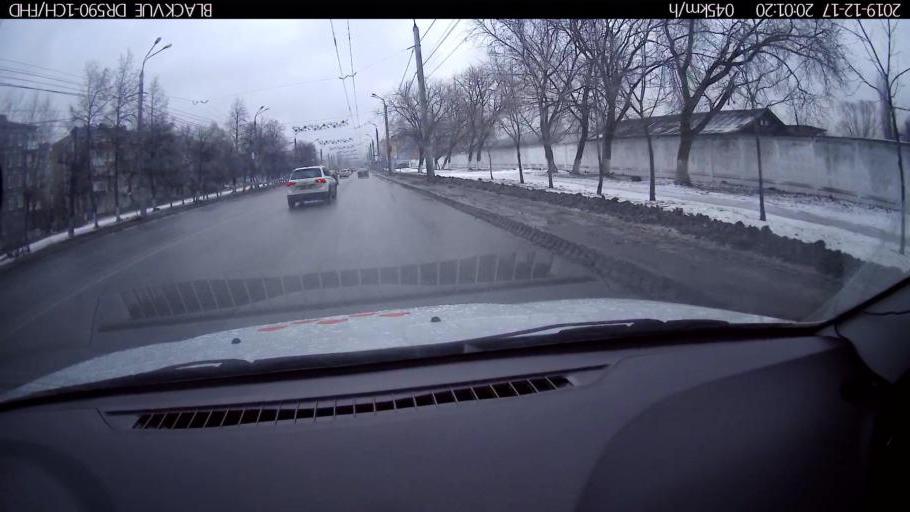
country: RU
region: Nizjnij Novgorod
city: Nizhniy Novgorod
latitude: 56.3228
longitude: 43.9196
